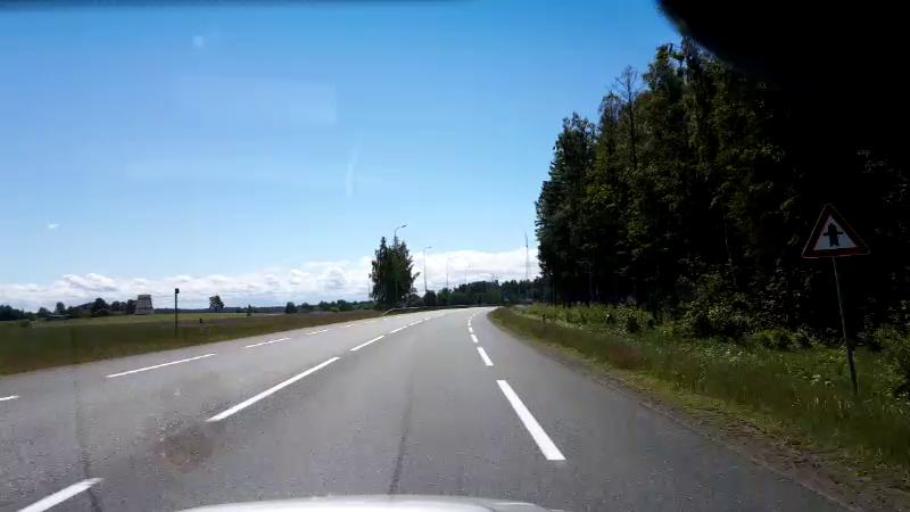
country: LV
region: Saulkrastu
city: Saulkrasti
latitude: 57.4074
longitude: 24.4320
